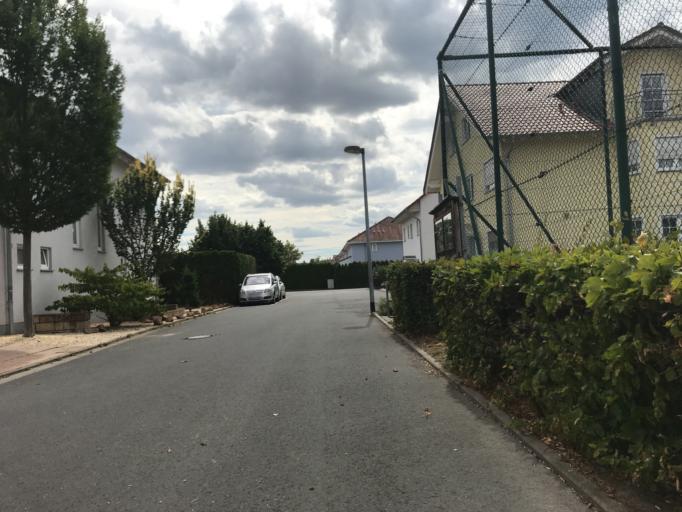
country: DE
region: Hesse
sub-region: Regierungsbezirk Darmstadt
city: Eltville
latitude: 50.0058
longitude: 8.1378
